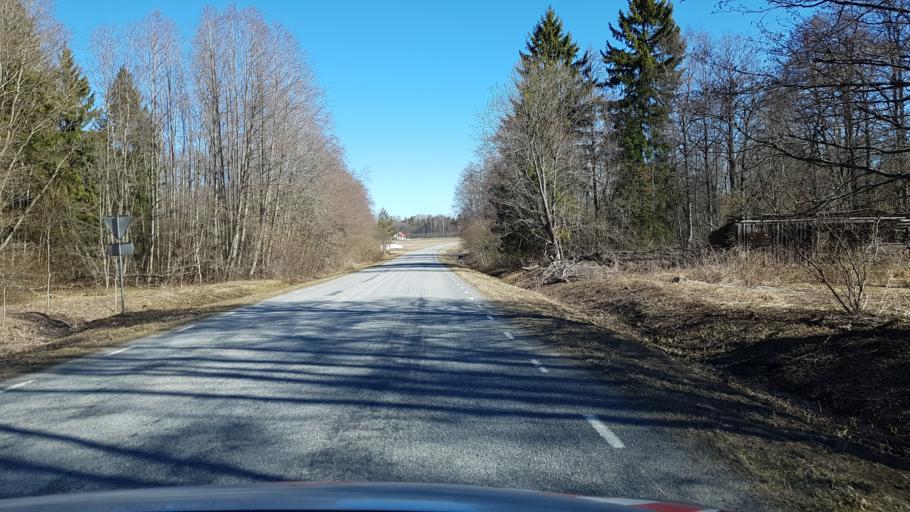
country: EE
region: Laeaene-Virumaa
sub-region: Haljala vald
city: Haljala
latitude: 59.4577
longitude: 26.2310
